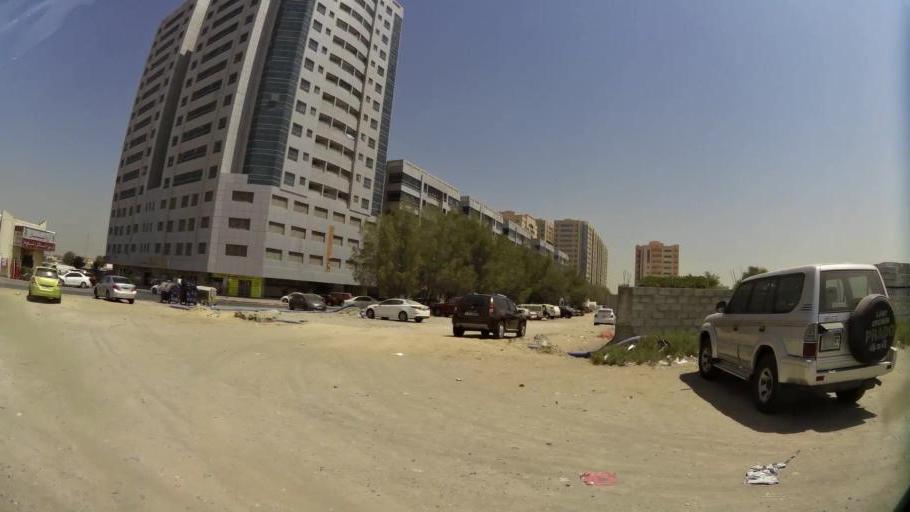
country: AE
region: Ajman
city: Ajman
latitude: 25.4016
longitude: 55.5073
